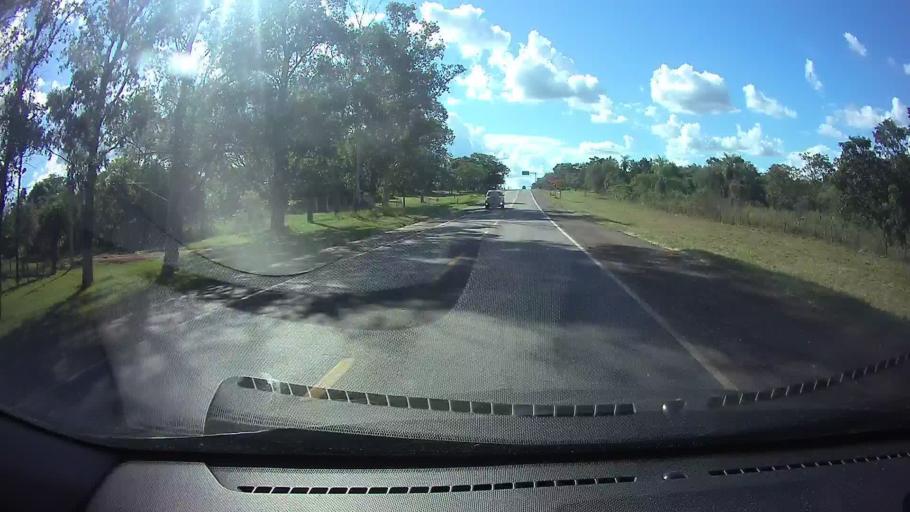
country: PY
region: Cordillera
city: Itacurubi de la Cordillera
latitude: -25.4566
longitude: -56.8938
